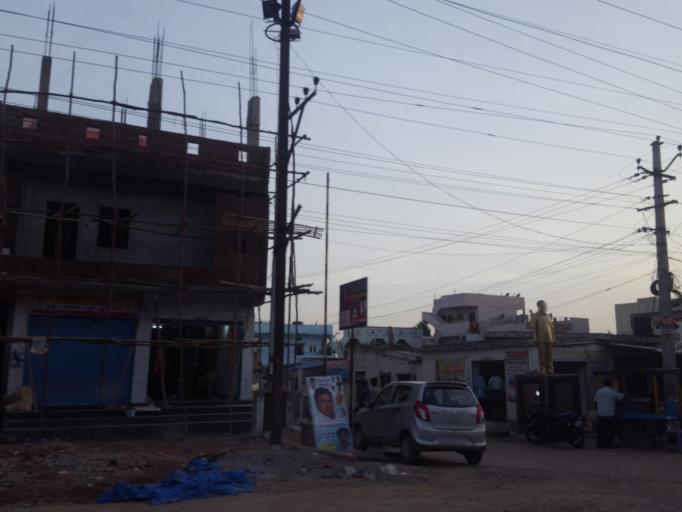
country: IN
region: Telangana
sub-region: Rangareddi
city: Kukatpalli
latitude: 17.5432
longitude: 78.3727
